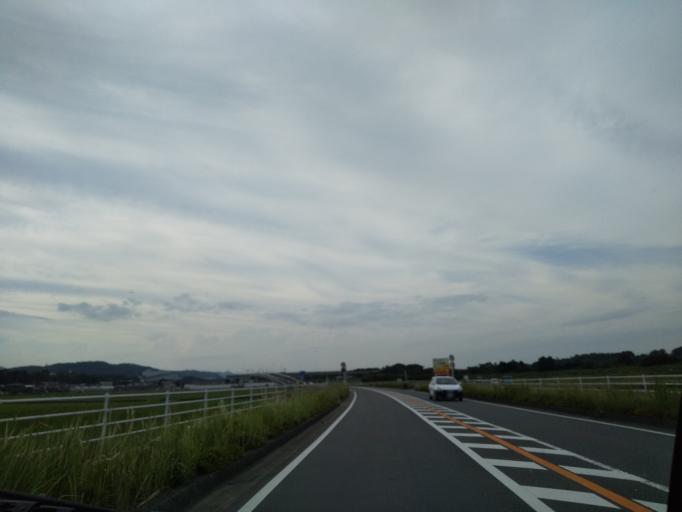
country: JP
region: Kanagawa
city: Zama
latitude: 35.4783
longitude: 139.3575
